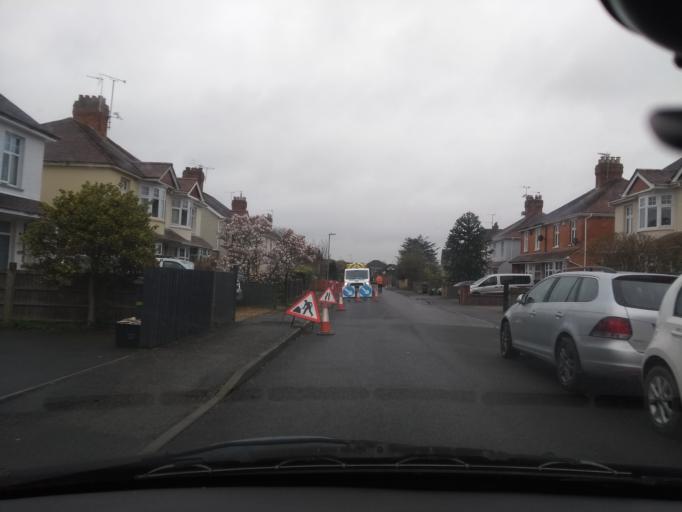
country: GB
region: England
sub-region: Somerset
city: Taunton
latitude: 51.0329
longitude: -3.1103
